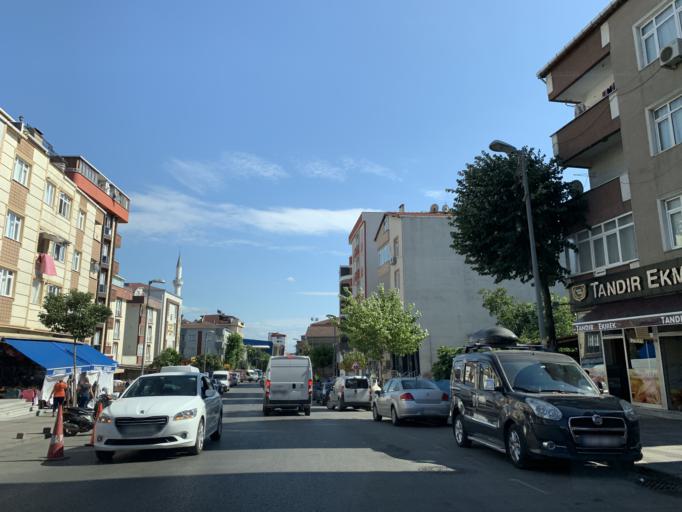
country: TR
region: Istanbul
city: Pendik
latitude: 40.8834
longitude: 29.2724
